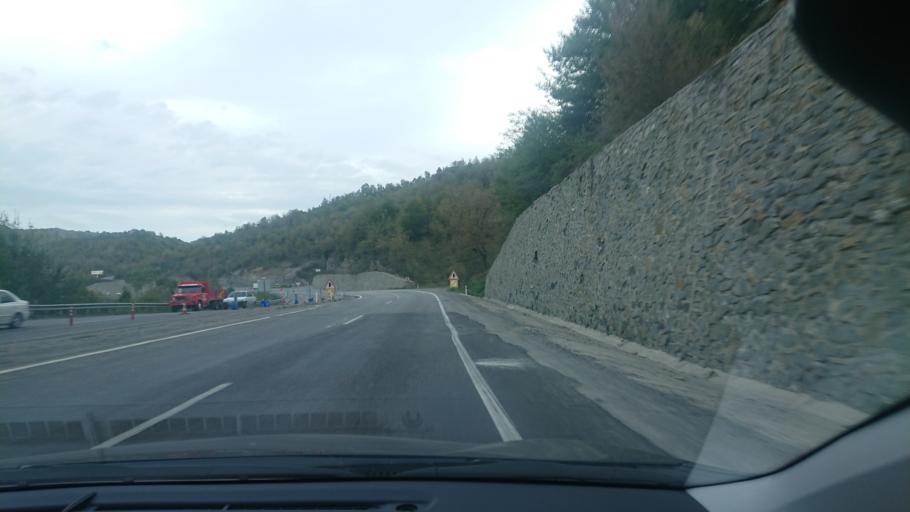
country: TR
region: Zonguldak
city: Beycuma
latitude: 41.4035
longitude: 31.9371
